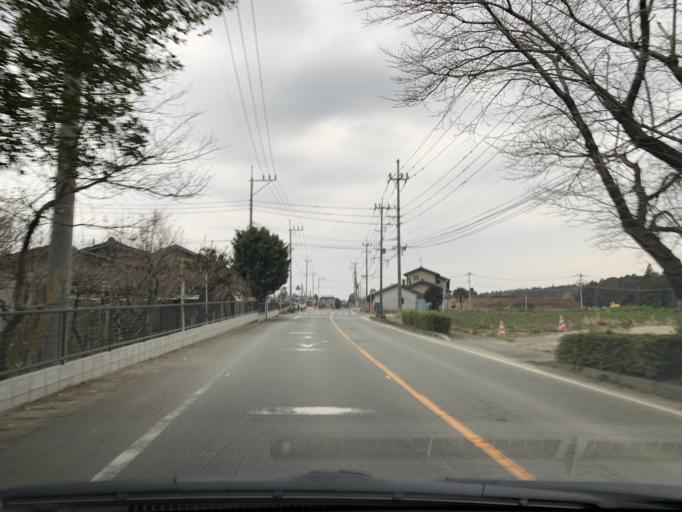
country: JP
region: Kumamoto
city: Ozu
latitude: 32.8901
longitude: 130.8980
